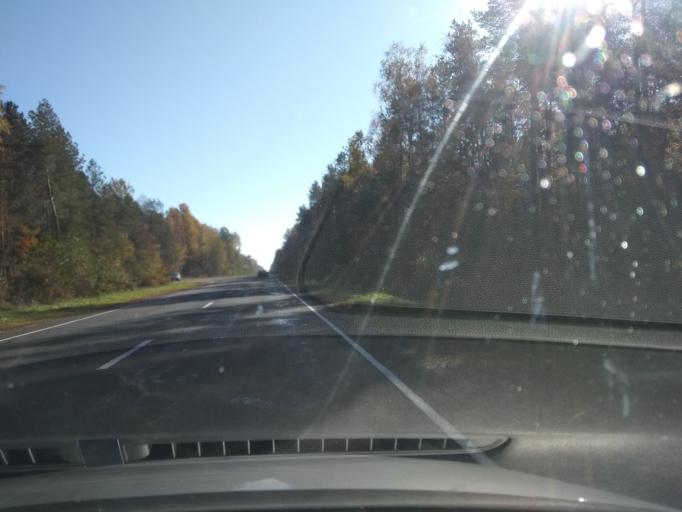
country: BY
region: Brest
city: Malaryta
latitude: 51.9060
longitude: 24.1120
